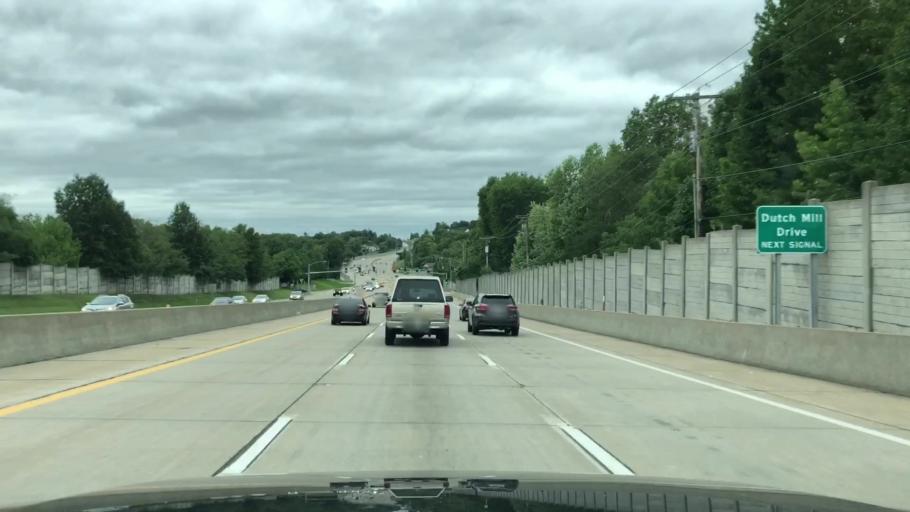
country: US
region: Missouri
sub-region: Saint Louis County
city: Manchester
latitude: 38.6135
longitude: -90.5122
